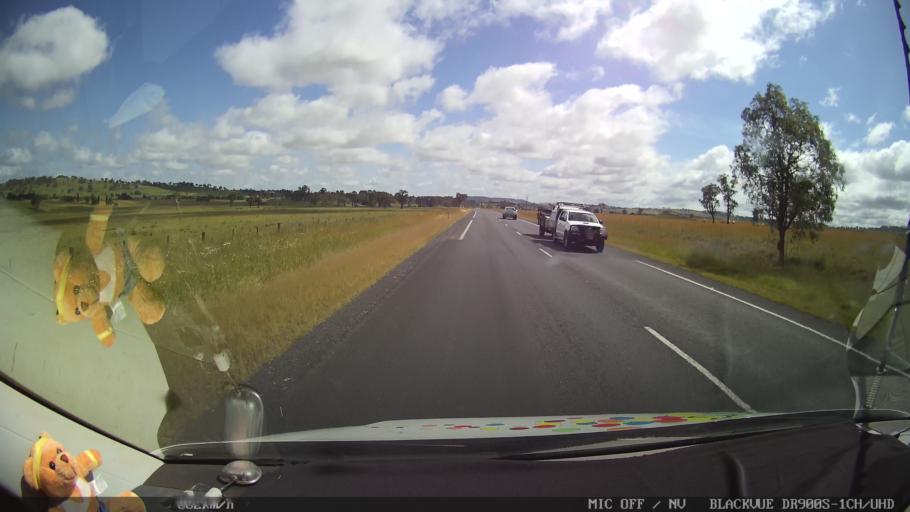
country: AU
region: New South Wales
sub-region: Glen Innes Severn
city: Glen Innes
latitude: -29.9438
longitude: 151.7214
